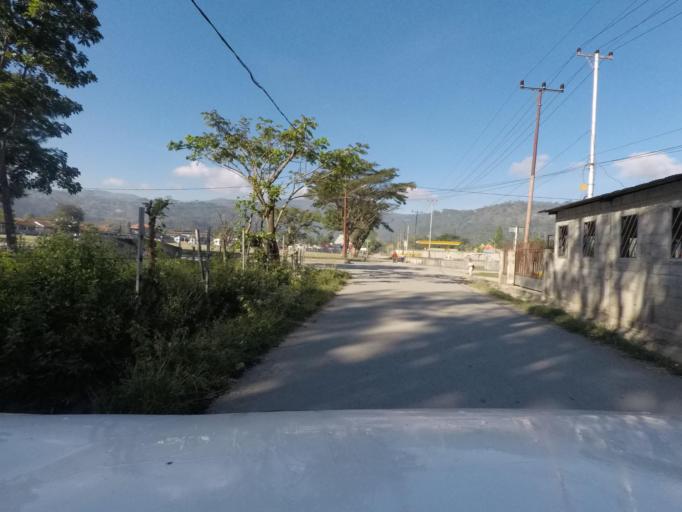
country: TL
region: Ermera
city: Gleno
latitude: -8.7226
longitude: 125.4317
